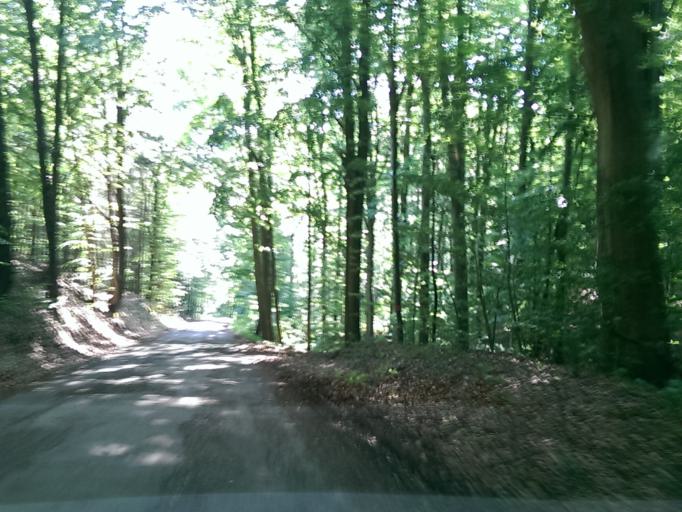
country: CZ
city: Duba
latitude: 50.4990
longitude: 14.5019
